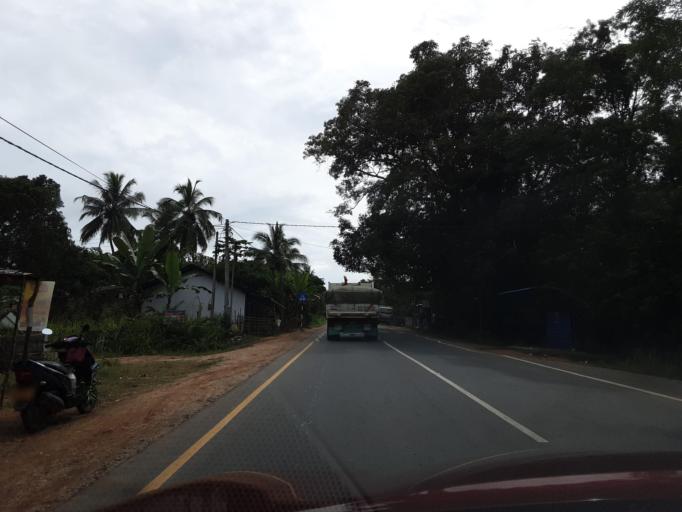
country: LK
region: Eastern Province
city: Eravur Town
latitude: 7.5242
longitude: 81.3467
